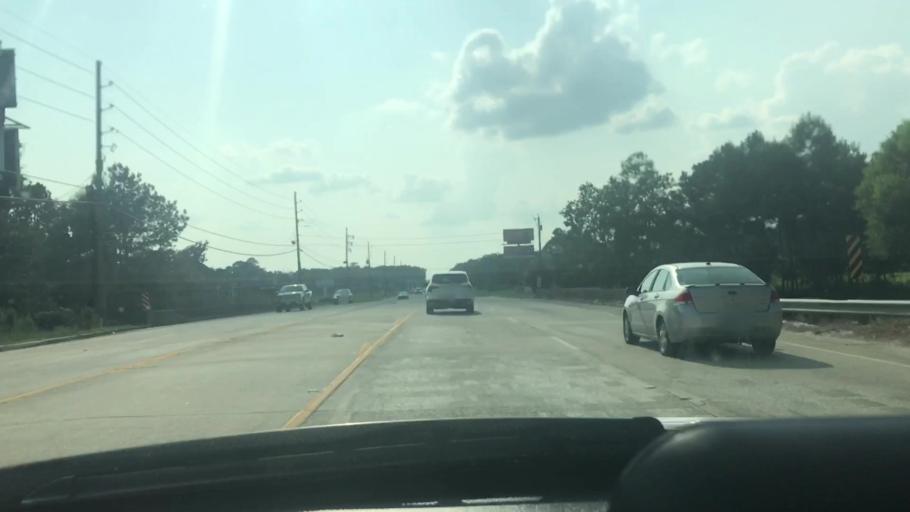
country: US
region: Louisiana
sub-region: Tangipahoa Parish
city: Natalbany
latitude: 30.5192
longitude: -90.4868
